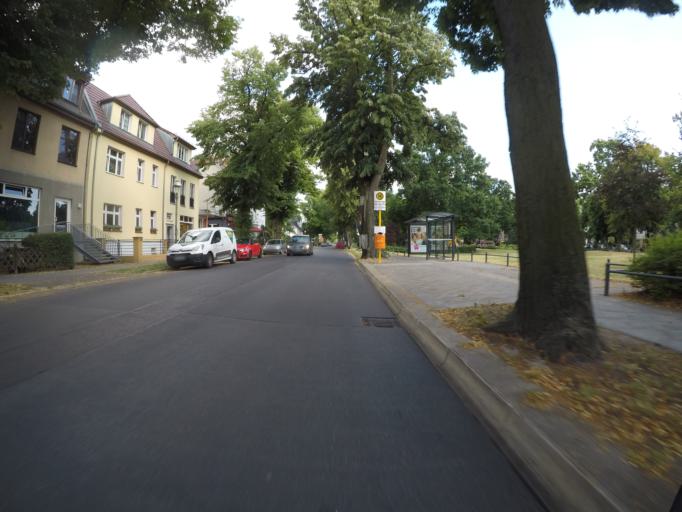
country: DE
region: Berlin
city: Kaulsdorf
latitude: 52.5108
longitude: 13.5878
